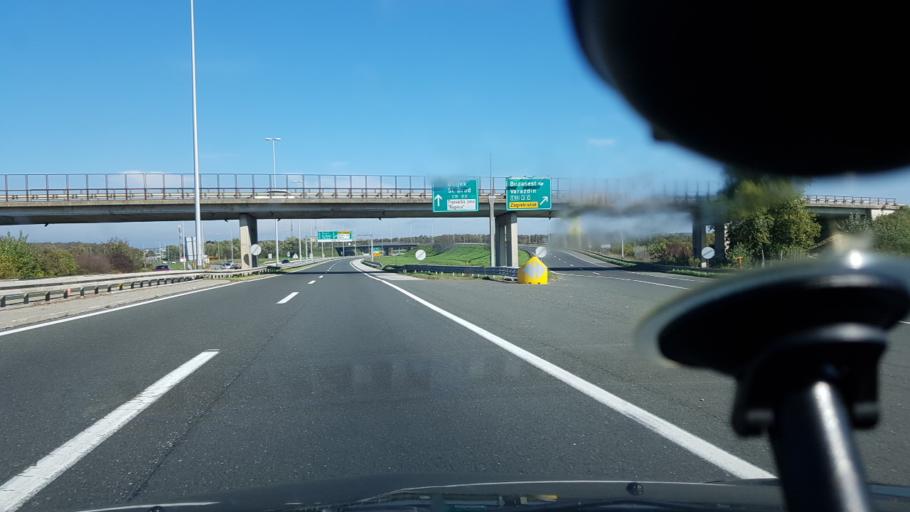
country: HR
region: Grad Zagreb
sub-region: Sesvete
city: Sesvete
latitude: 45.7917
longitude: 16.1275
